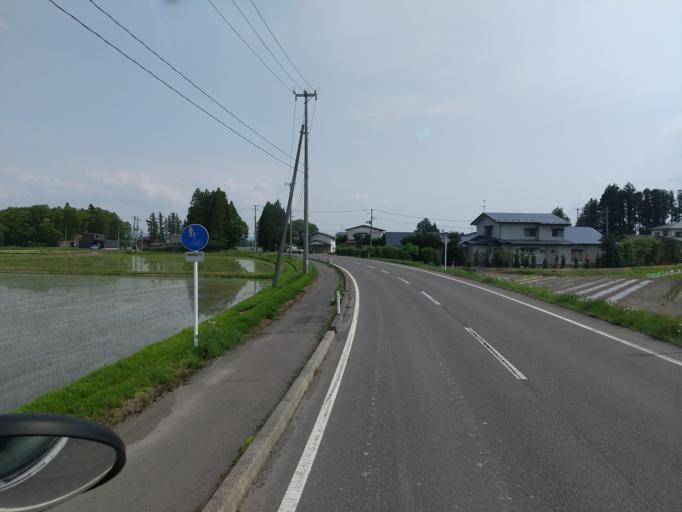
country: JP
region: Iwate
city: Hanamaki
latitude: 39.3990
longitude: 141.0884
